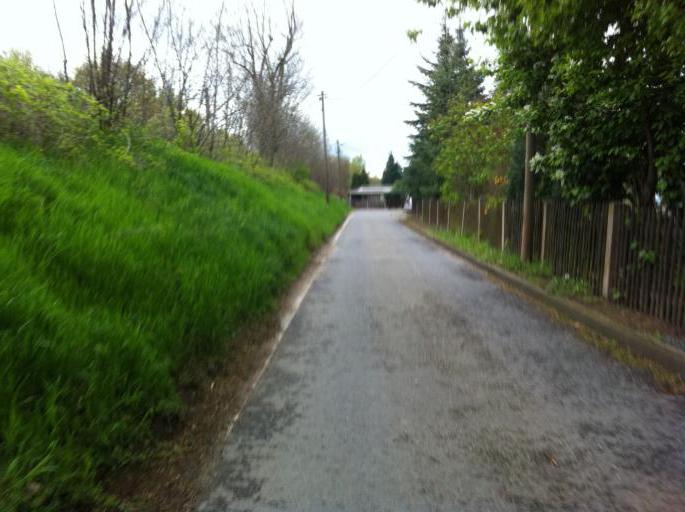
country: DE
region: Saxony
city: Weinbohla
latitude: 51.1502
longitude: 13.5646
